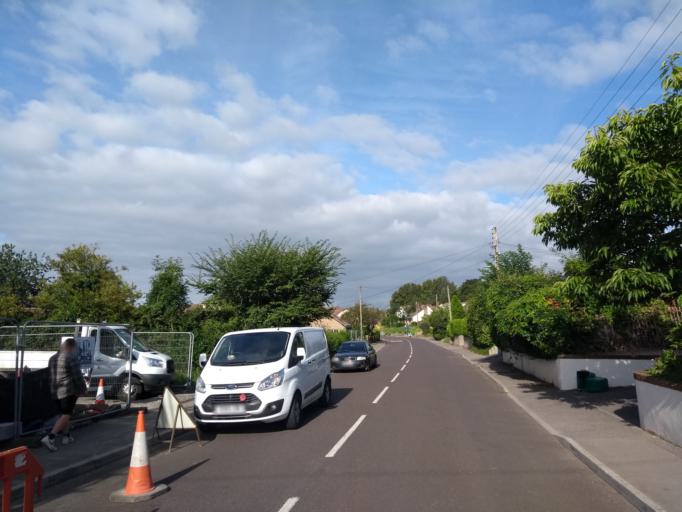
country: GB
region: England
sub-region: Somerset
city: Axbridge
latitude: 51.2871
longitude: -2.8098
